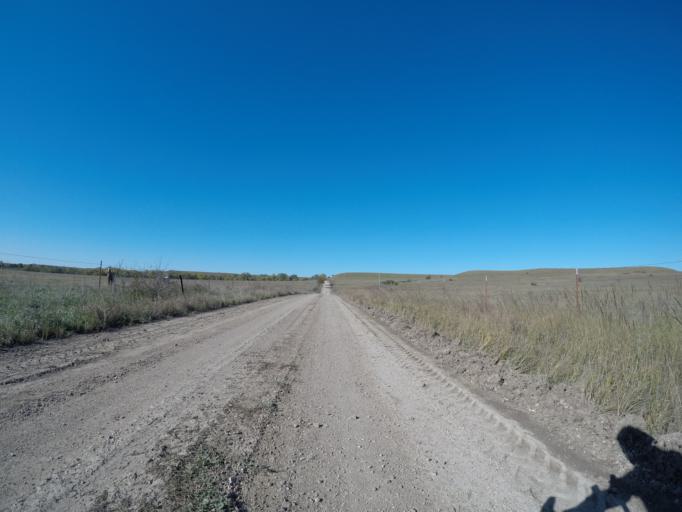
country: US
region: Kansas
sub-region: Wabaunsee County
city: Alma
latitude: 38.9132
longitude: -96.3683
